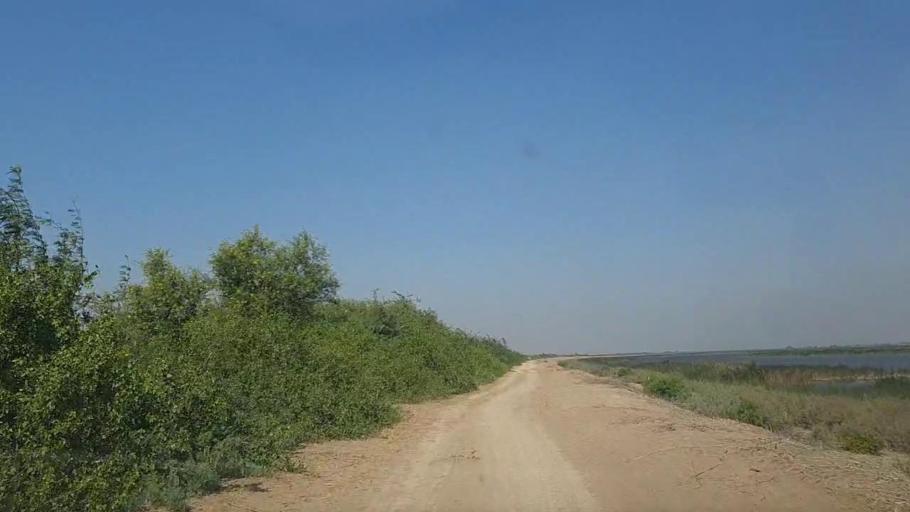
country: PK
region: Sindh
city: Daro Mehar
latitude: 24.9176
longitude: 68.0784
